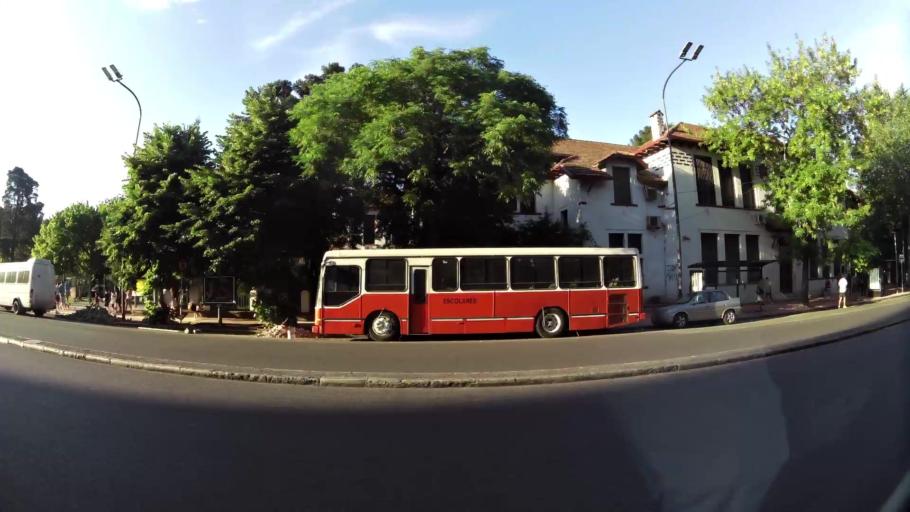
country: AR
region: Buenos Aires F.D.
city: Colegiales
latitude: -34.6087
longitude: -58.4351
